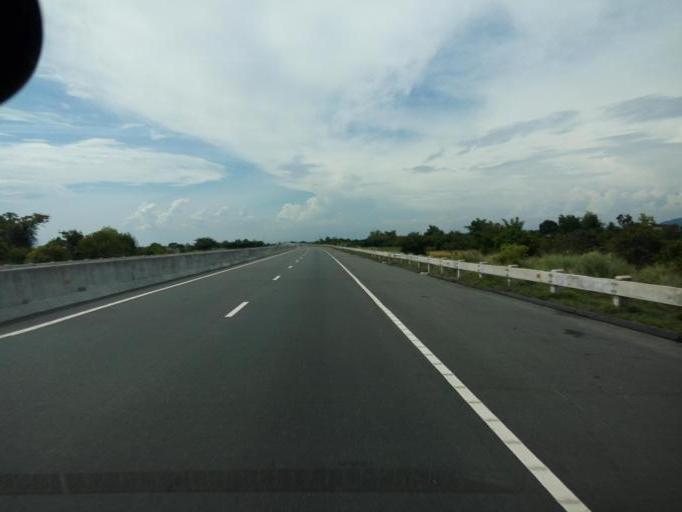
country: PH
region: Central Luzon
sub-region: Province of Nueva Ecija
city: Calancuasan Norte
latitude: 15.7961
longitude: 120.6412
